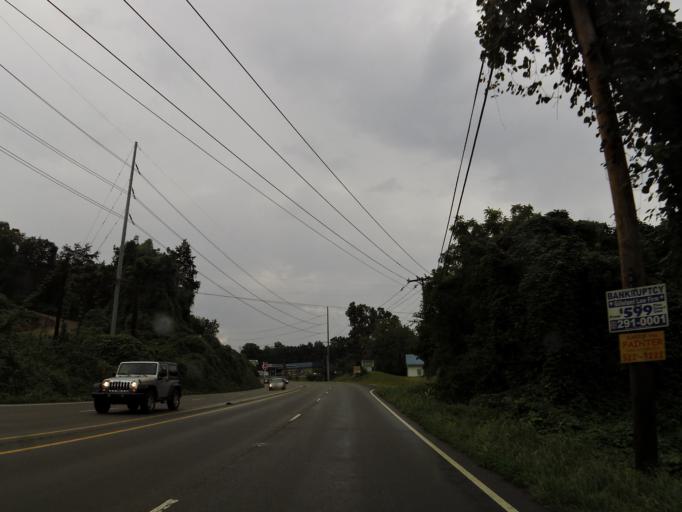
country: US
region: Tennessee
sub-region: Sevier County
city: Seymour
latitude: 35.8974
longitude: -83.8125
